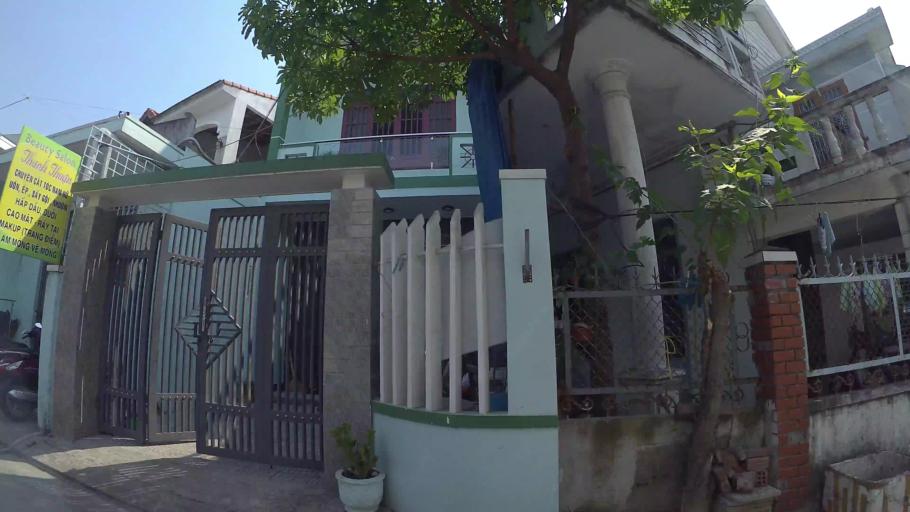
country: VN
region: Da Nang
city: Cam Le
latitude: 16.0146
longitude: 108.2013
